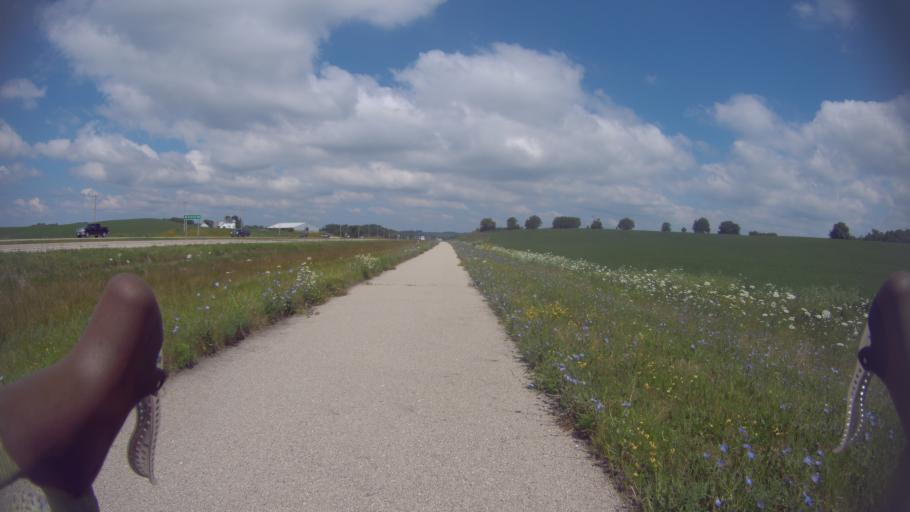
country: US
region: Wisconsin
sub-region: Dane County
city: Waunakee
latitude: 43.1821
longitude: -89.5480
